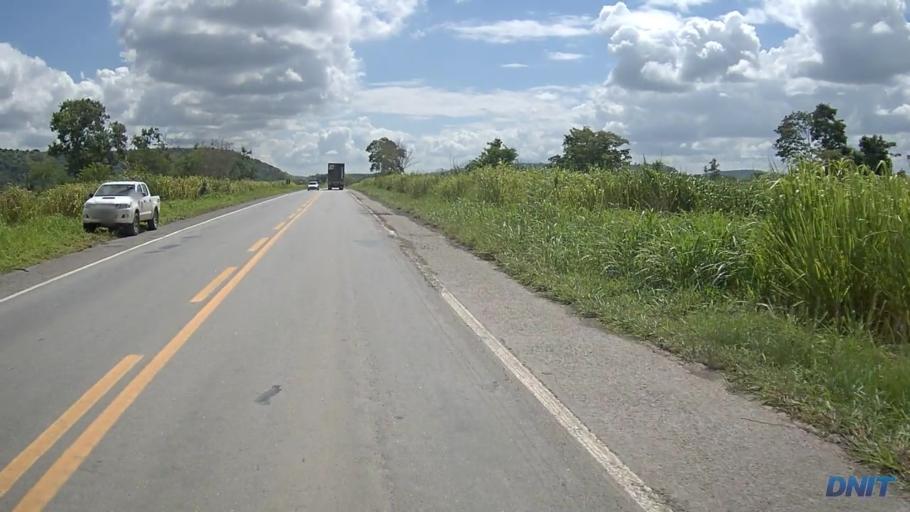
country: BR
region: Minas Gerais
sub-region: Governador Valadares
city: Governador Valadares
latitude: -19.0074
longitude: -42.1336
